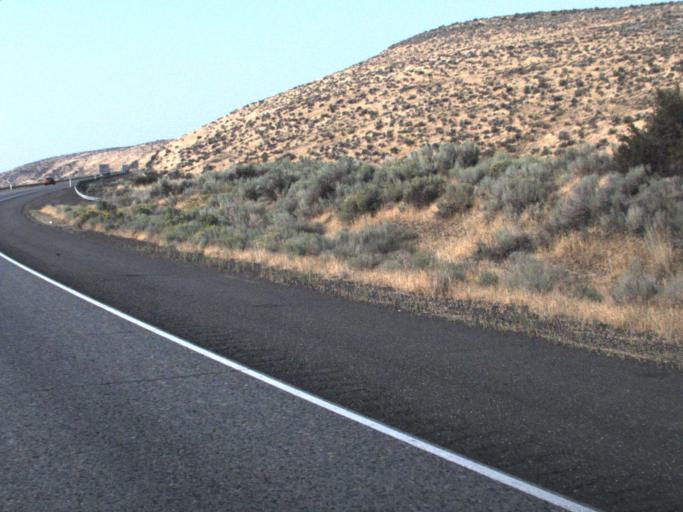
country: US
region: Washington
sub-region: Kittitas County
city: Kittitas
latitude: 46.7917
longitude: -120.3597
